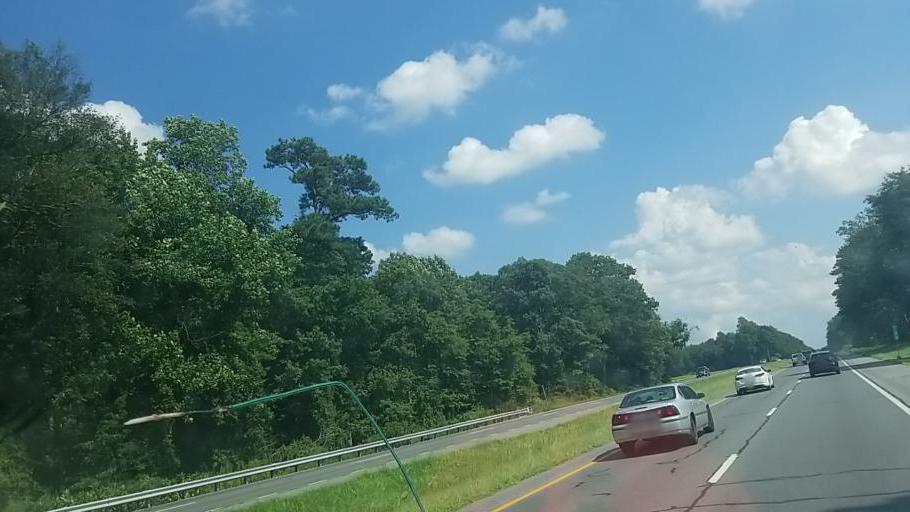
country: US
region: Delaware
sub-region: Sussex County
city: Millsboro
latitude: 38.6139
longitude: -75.3315
